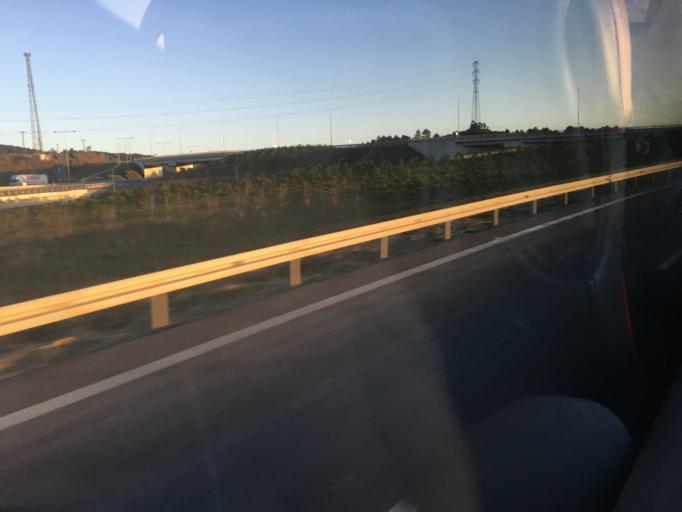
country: TR
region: Istanbul
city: Sancaktepe
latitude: 41.0525
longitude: 29.2757
